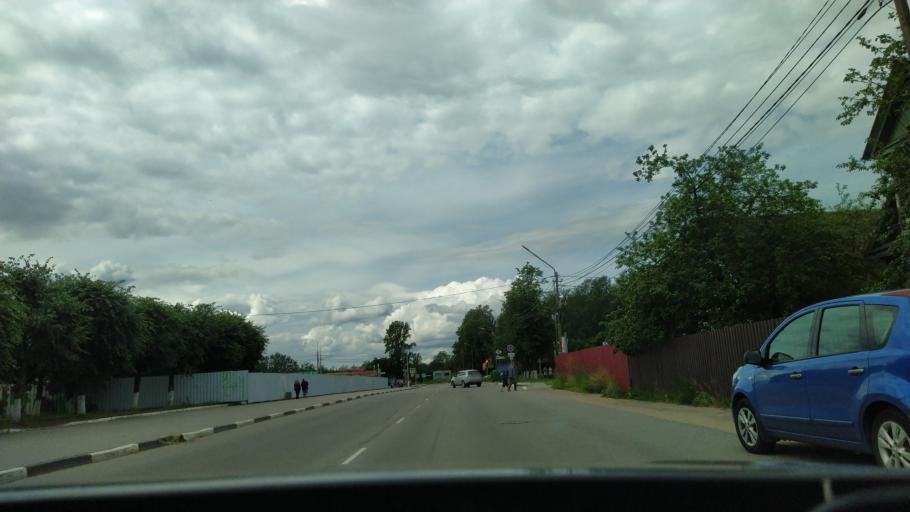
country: RU
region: Leningrad
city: Kirovsk
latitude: 59.8818
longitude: 30.9863
